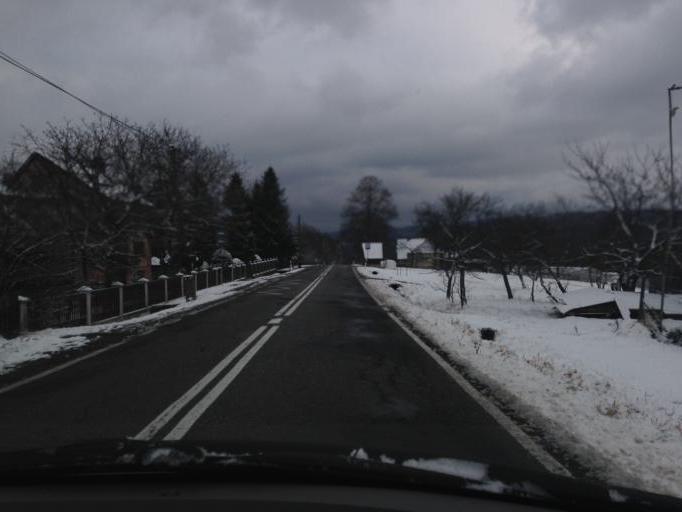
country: PL
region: Lesser Poland Voivodeship
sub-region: Powiat bochenski
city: Nowy Wisnicz
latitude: 49.8503
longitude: 20.4906
